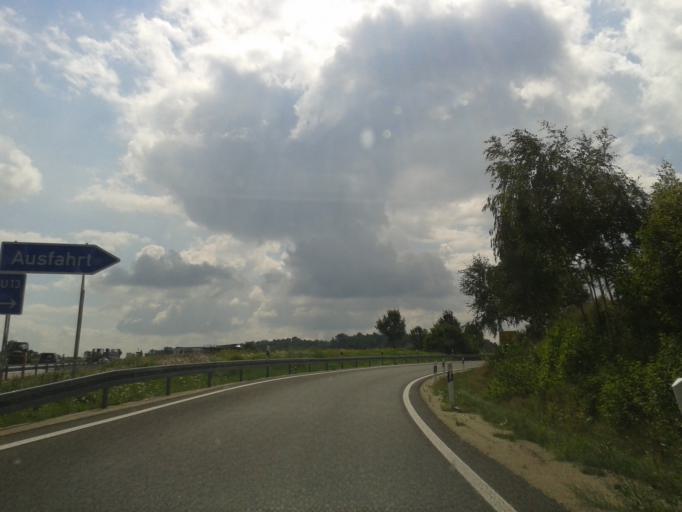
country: DE
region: Saxony
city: Goda
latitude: 51.1931
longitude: 14.3569
